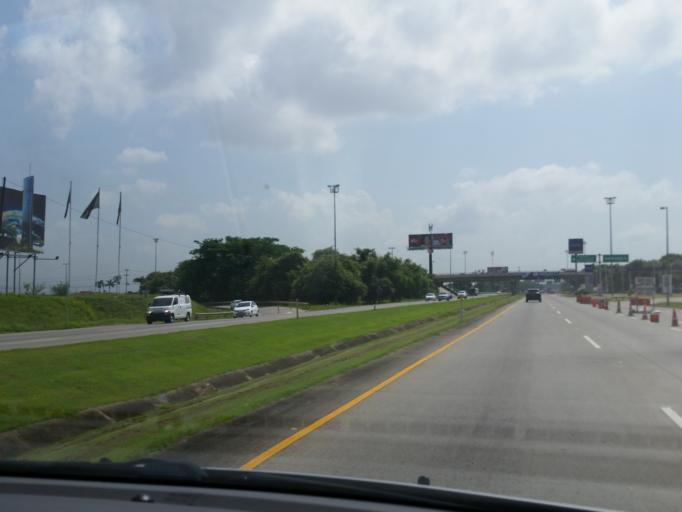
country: PA
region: Panama
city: San Miguelito
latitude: 9.0286
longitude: -79.4577
